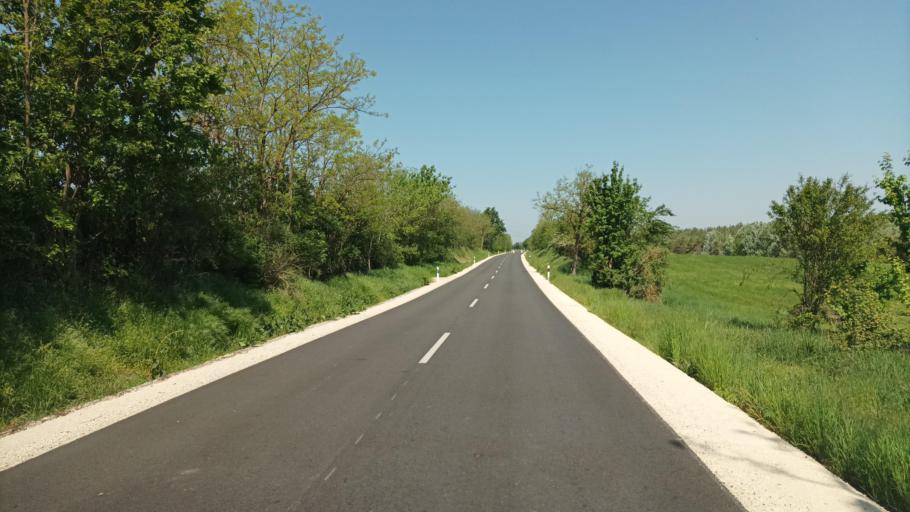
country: HU
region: Pest
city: Gomba
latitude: 47.3802
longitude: 19.5121
